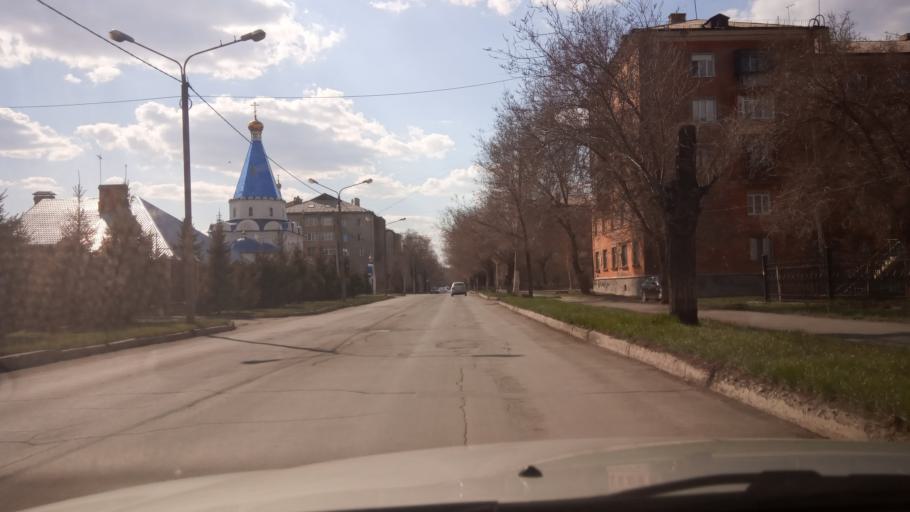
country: RU
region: Orenburg
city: Novotroitsk
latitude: 51.1941
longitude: 58.3086
